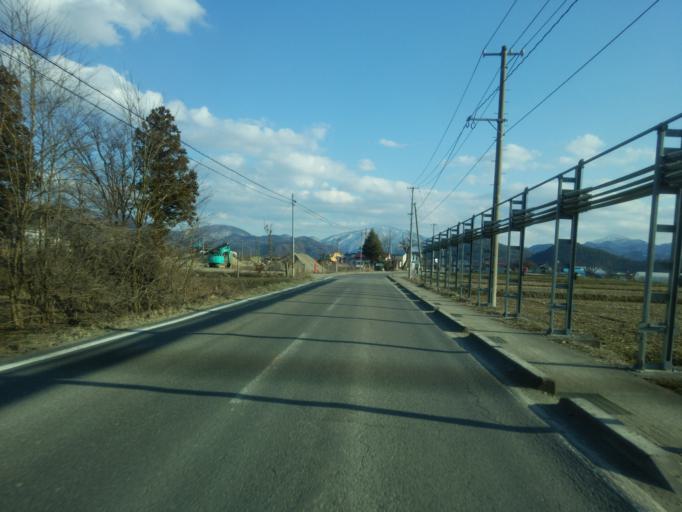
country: JP
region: Fukushima
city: Kitakata
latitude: 37.4694
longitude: 139.8964
